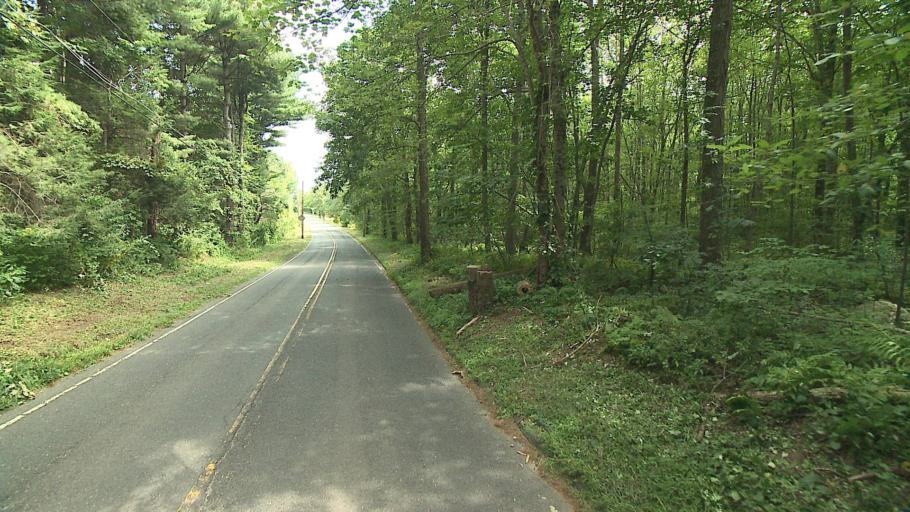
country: US
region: Connecticut
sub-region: Litchfield County
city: Bethlehem Village
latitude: 41.6438
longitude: -73.1643
